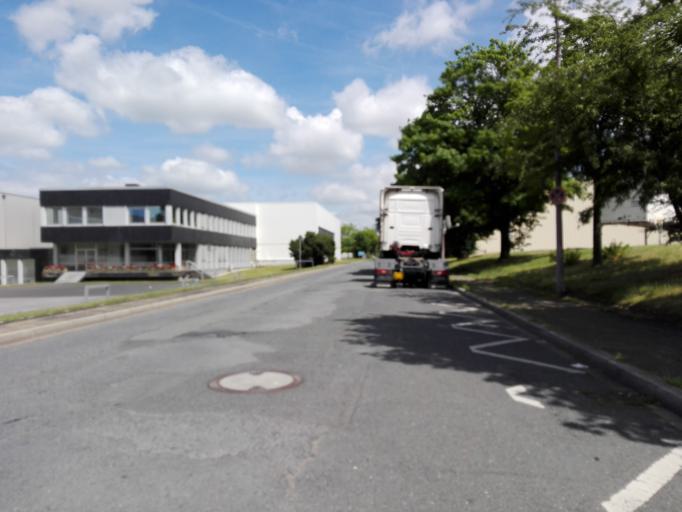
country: DE
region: North Rhine-Westphalia
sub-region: Regierungsbezirk Arnsberg
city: Unna
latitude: 51.5297
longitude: 7.7165
